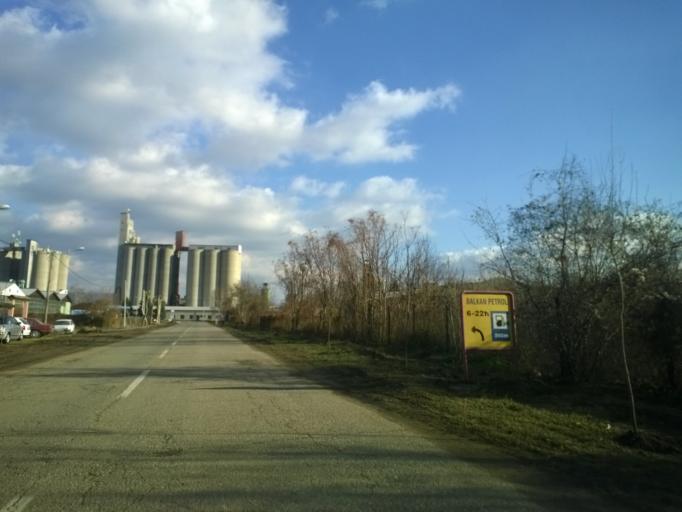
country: RS
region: Central Serbia
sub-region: Branicevski Okrug
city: Veliko Gradiste
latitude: 44.7552
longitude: 21.5137
